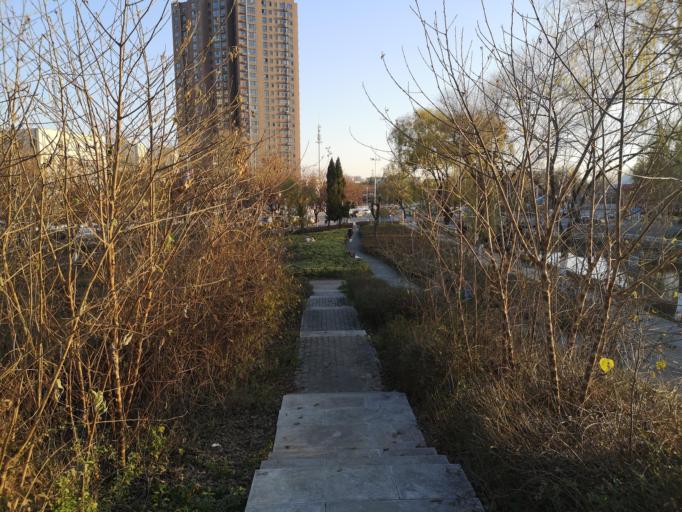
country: CN
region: Henan Sheng
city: Puyang
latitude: 35.7635
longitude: 115.0038
